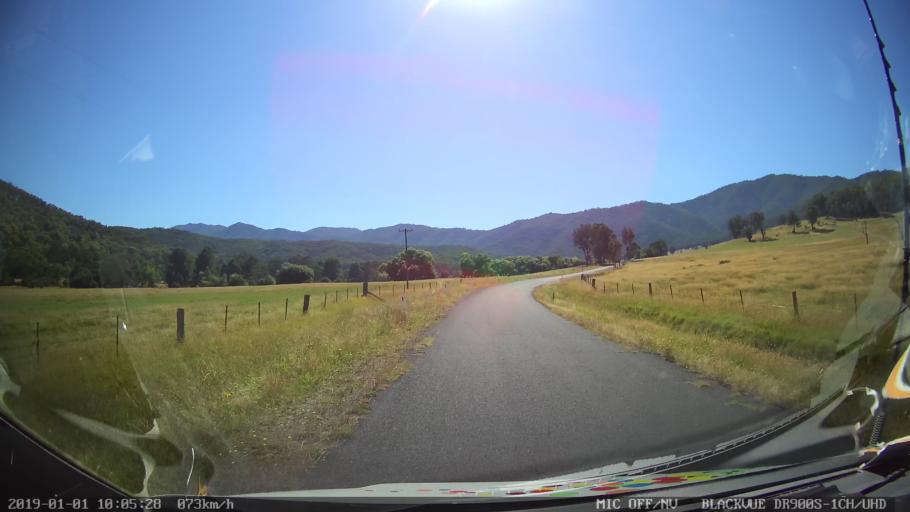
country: AU
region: New South Wales
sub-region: Snowy River
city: Jindabyne
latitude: -36.1737
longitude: 148.1360
